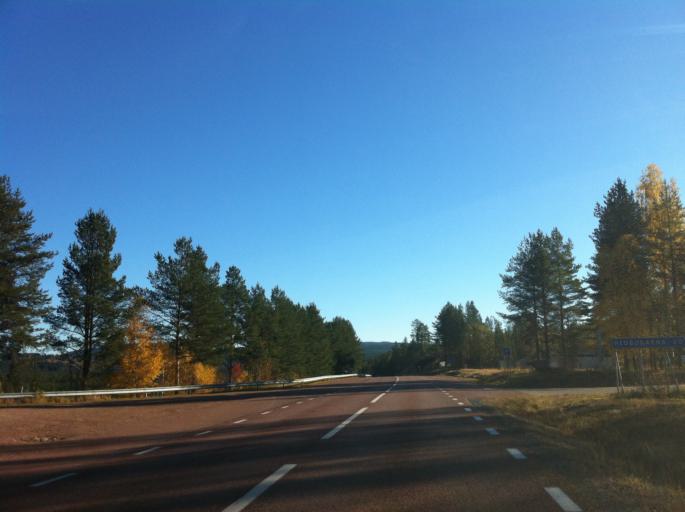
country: SE
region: Dalarna
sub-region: Alvdalens Kommun
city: AElvdalen
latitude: 61.2992
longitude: 13.7292
